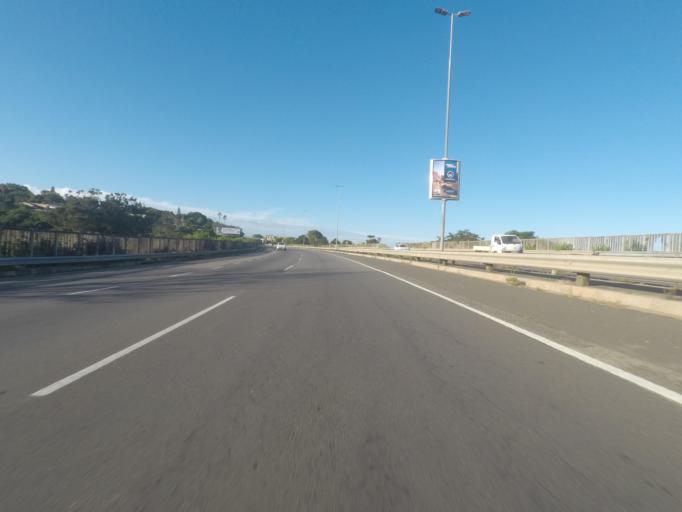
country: ZA
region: Eastern Cape
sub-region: Buffalo City Metropolitan Municipality
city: East London
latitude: -32.9895
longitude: 27.9193
